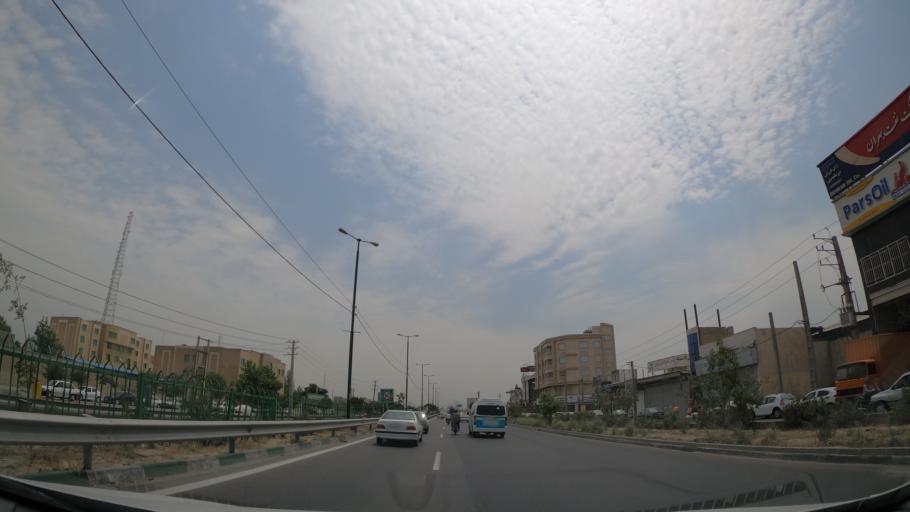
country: IR
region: Tehran
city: Eslamshahr
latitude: 35.6769
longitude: 51.2733
